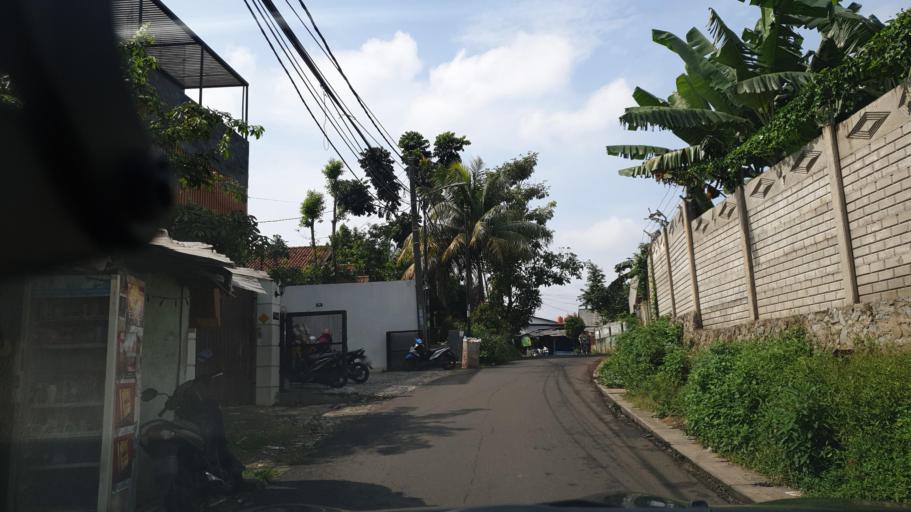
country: ID
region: West Java
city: Pamulang
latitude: -6.3207
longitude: 106.7553
